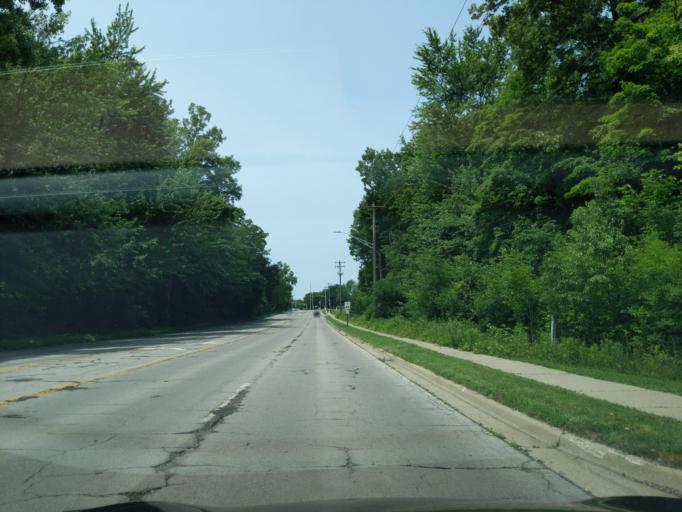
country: US
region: Michigan
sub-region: Eaton County
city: Waverly
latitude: 42.7338
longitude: -84.6371
